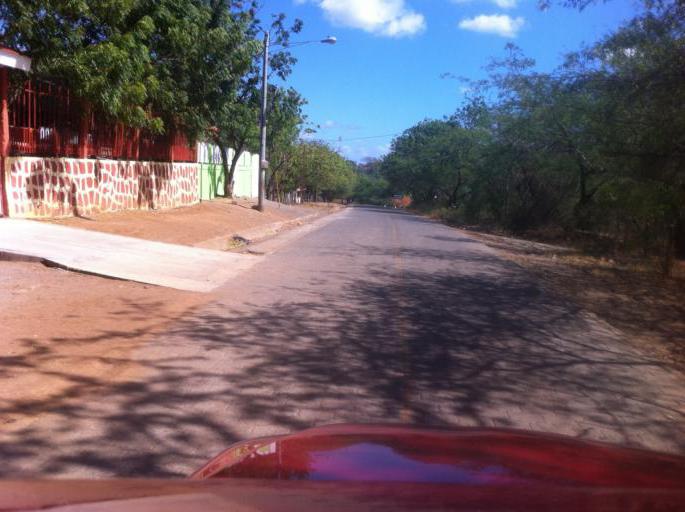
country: NI
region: Carazo
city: El Rosario
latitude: 11.6209
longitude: -86.3291
